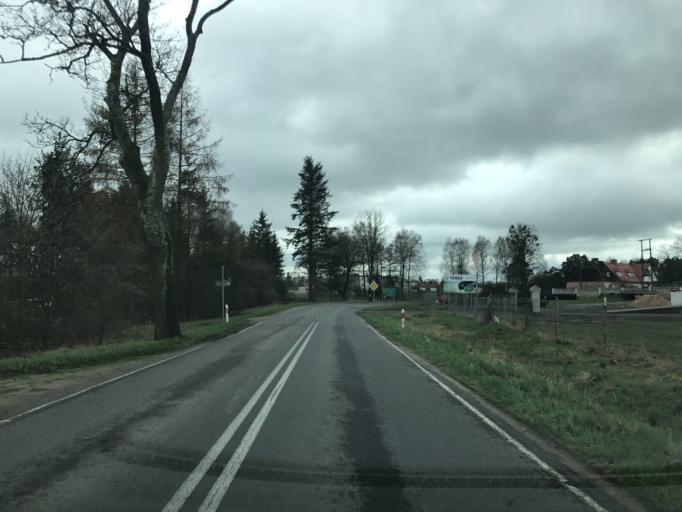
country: PL
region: Warmian-Masurian Voivodeship
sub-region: Powiat ostrodzki
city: Gierzwald
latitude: 53.5014
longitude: 20.1721
